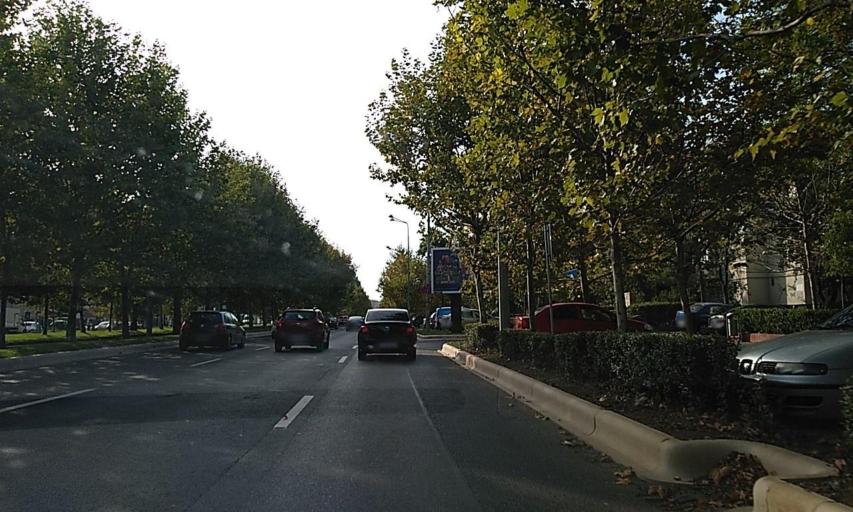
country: RO
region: Ilfov
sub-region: Comuna Popesti-Leordeni
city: Popesti-Leordeni
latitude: 44.4107
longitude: 26.1828
